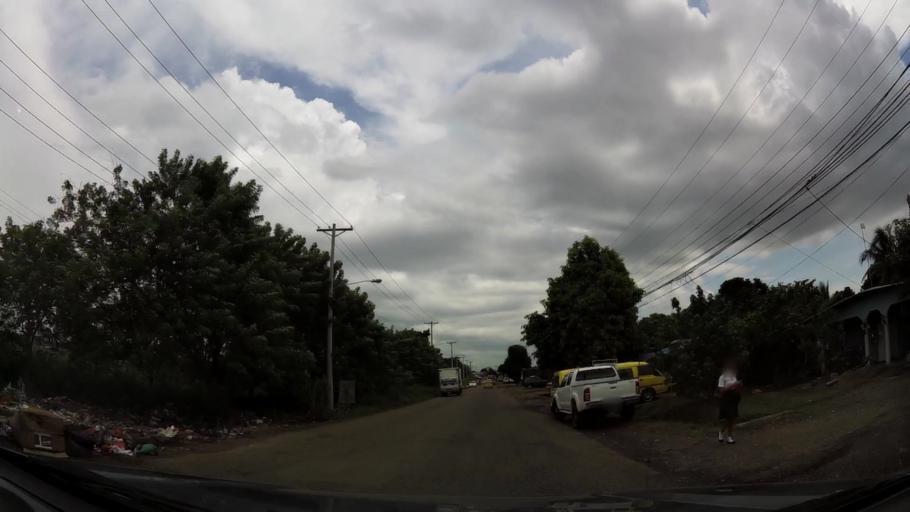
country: PA
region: Panama
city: Cabra Numero Uno
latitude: 9.1117
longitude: -79.3246
